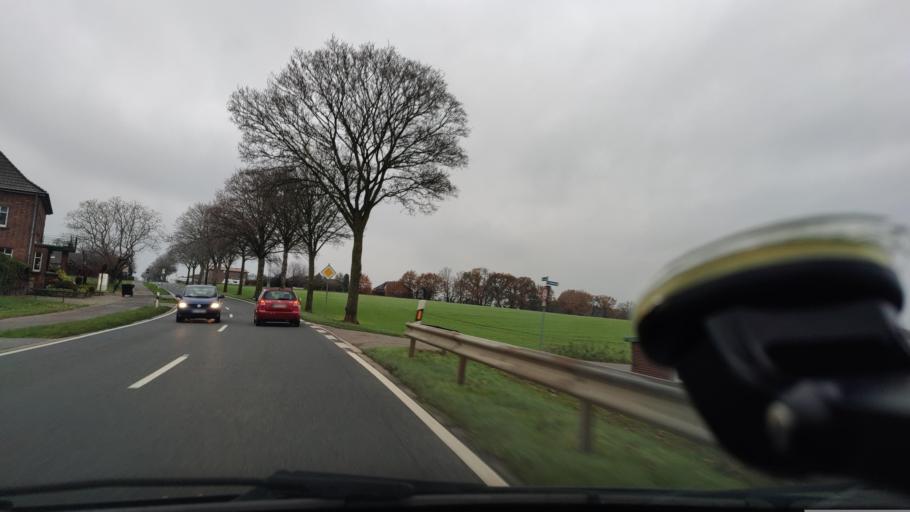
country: DE
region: North Rhine-Westphalia
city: Kalkar
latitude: 51.7241
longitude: 6.2900
